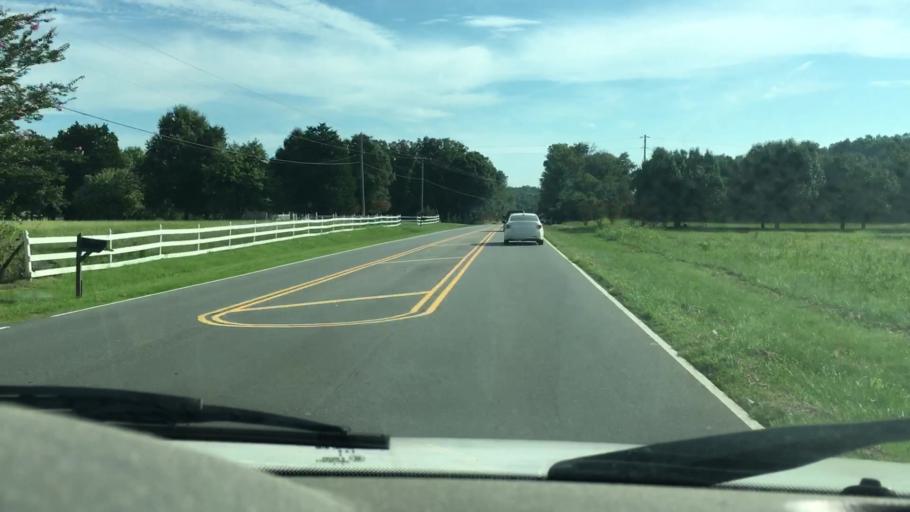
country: US
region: North Carolina
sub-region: Mecklenburg County
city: Huntersville
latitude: 35.3759
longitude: -80.8010
